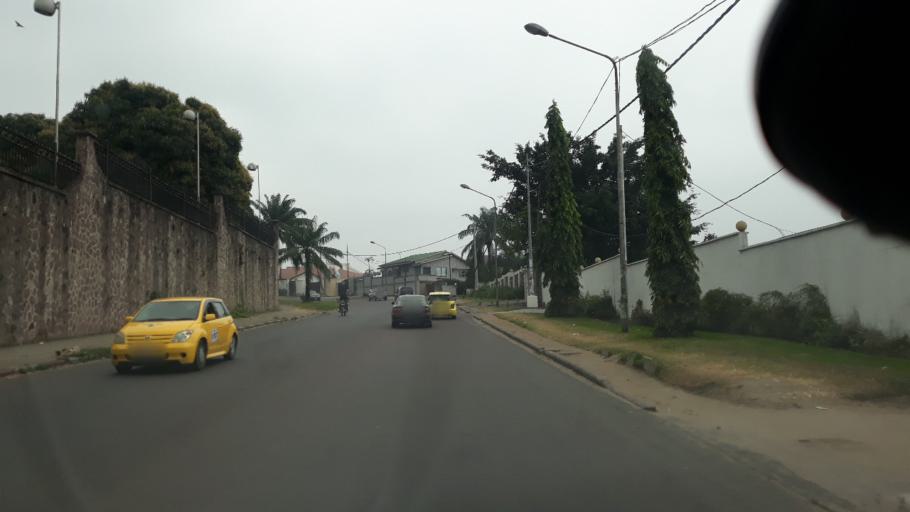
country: CD
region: Kinshasa
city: Kinshasa
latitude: -4.3626
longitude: 15.2505
